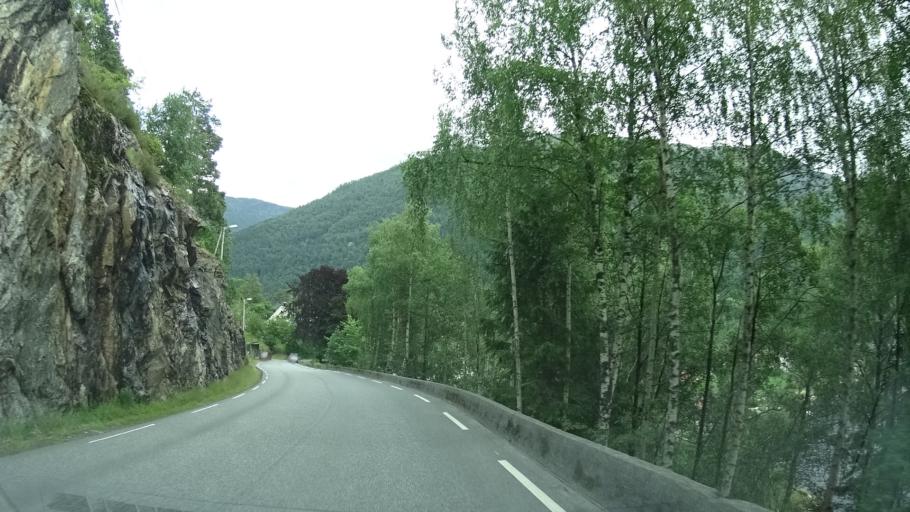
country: NO
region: Hordaland
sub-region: Jondal
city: Jondal
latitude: 60.2822
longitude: 6.2483
